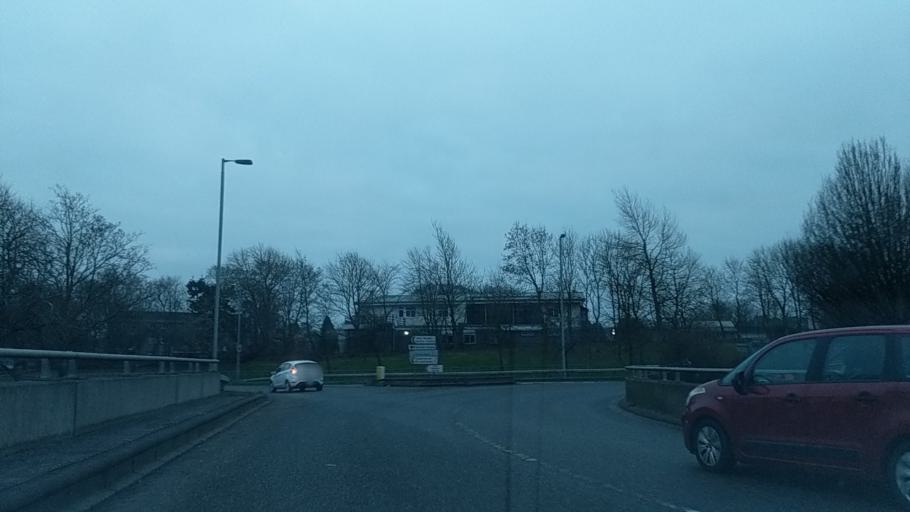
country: GB
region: Scotland
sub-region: South Lanarkshire
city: East Kilbride
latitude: 55.7635
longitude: -4.1655
